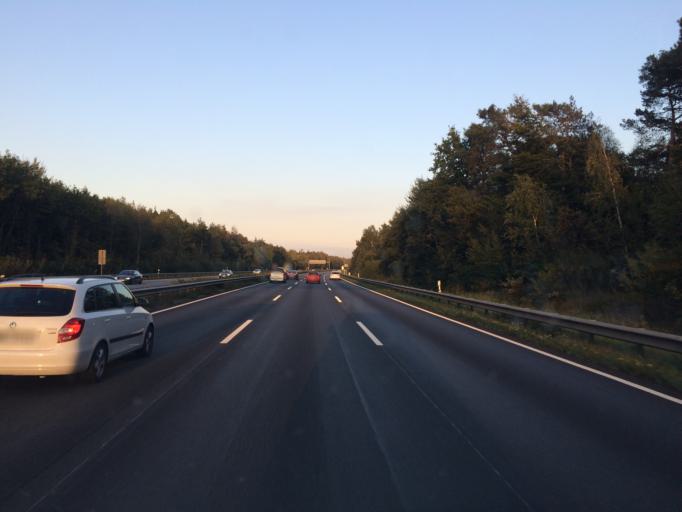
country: DE
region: Rheinland-Pfalz
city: Rodenbach
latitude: 49.4426
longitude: 7.6596
